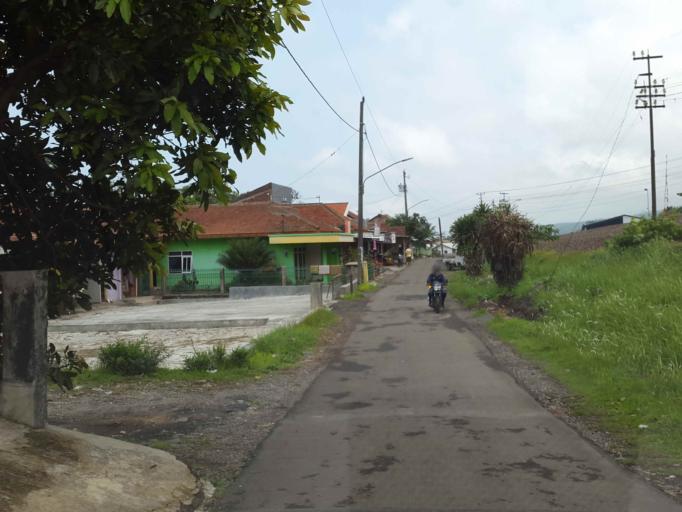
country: ID
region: Central Java
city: Muara
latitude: -7.2898
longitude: 109.0295
